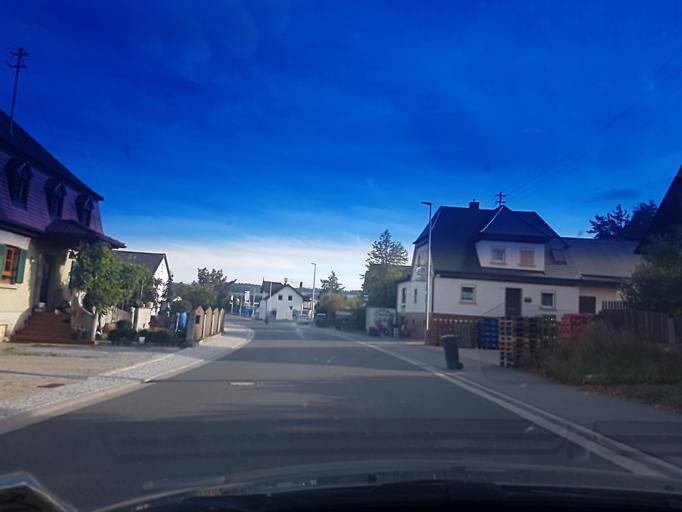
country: DE
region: Bavaria
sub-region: Regierungsbezirk Mittelfranken
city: Burghaslach
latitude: 49.7708
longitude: 10.5628
